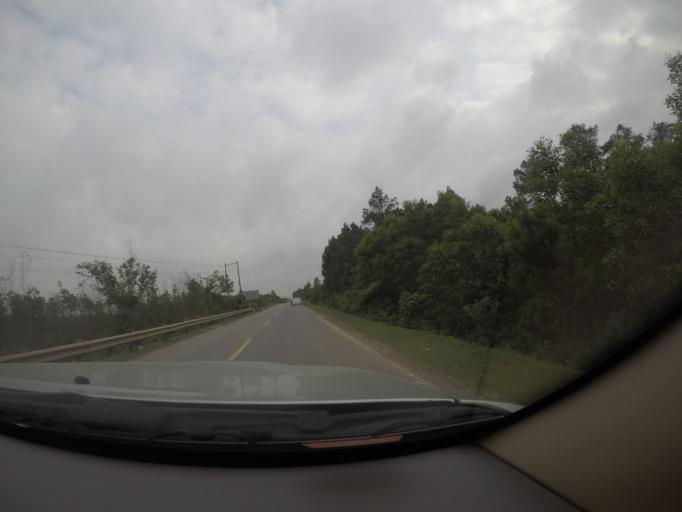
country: VN
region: Quang Binh
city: Quan Hau
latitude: 17.4018
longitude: 106.6066
